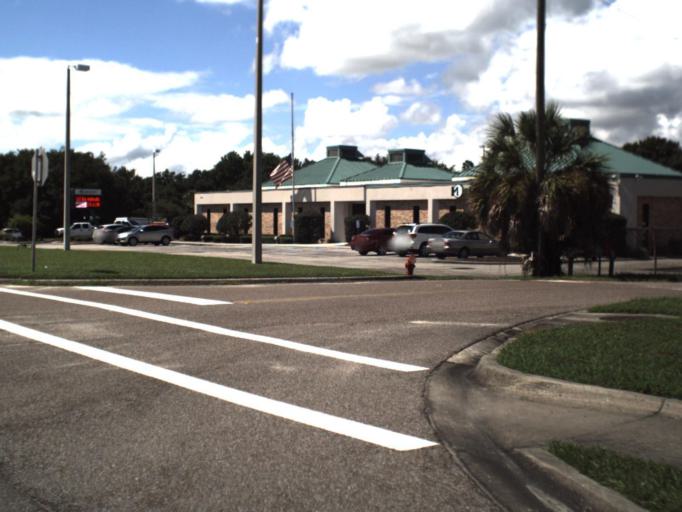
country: US
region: Florida
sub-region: Polk County
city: Mulberry
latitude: 27.9042
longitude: -81.9738
